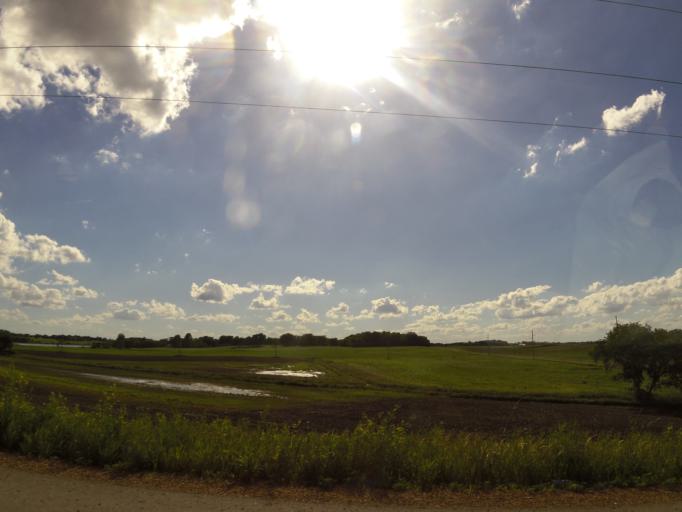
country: US
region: Minnesota
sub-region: Carver County
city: Waconia
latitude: 44.8900
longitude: -93.8186
